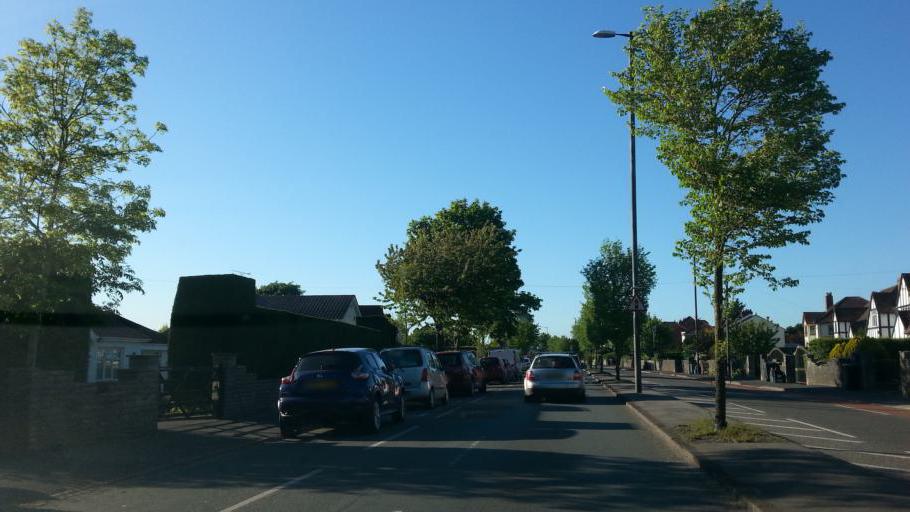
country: GB
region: England
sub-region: Bath and North East Somerset
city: Whitchurch
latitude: 51.4197
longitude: -2.5609
